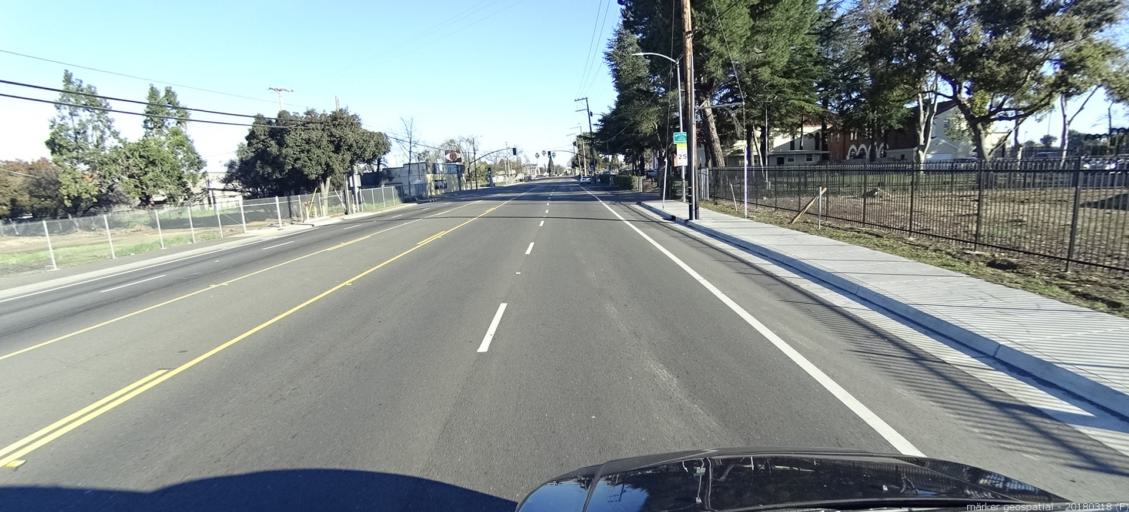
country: US
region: California
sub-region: Sacramento County
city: Parkway
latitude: 38.5172
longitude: -121.4695
